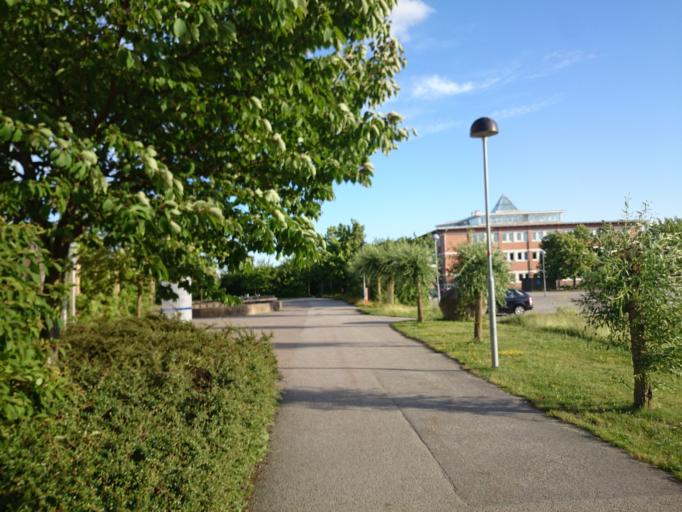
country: SE
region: Skane
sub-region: Lunds Kommun
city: Lund
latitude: 55.7117
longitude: 13.2147
